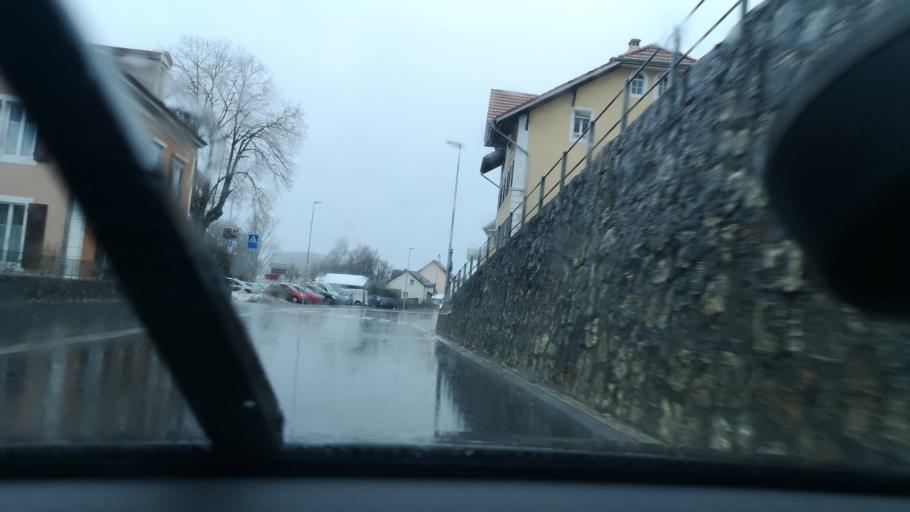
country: CH
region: Neuchatel
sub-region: Val-de-Travers District
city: Travers
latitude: 46.9389
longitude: 6.6730
